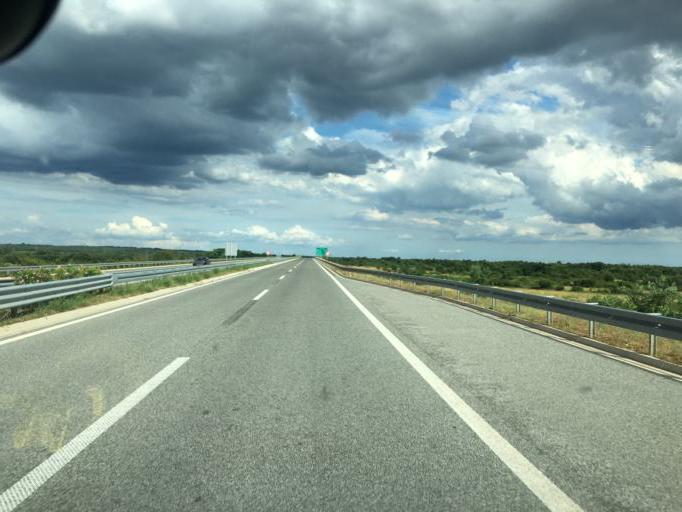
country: HR
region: Istarska
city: Vodnjan
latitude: 44.9842
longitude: 13.8513
